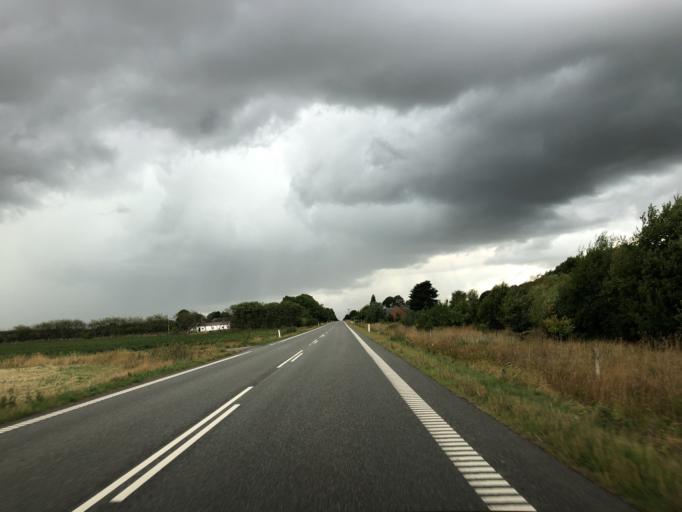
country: DK
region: Central Jutland
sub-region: Ikast-Brande Kommune
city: Bording Kirkeby
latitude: 56.1370
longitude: 9.3406
